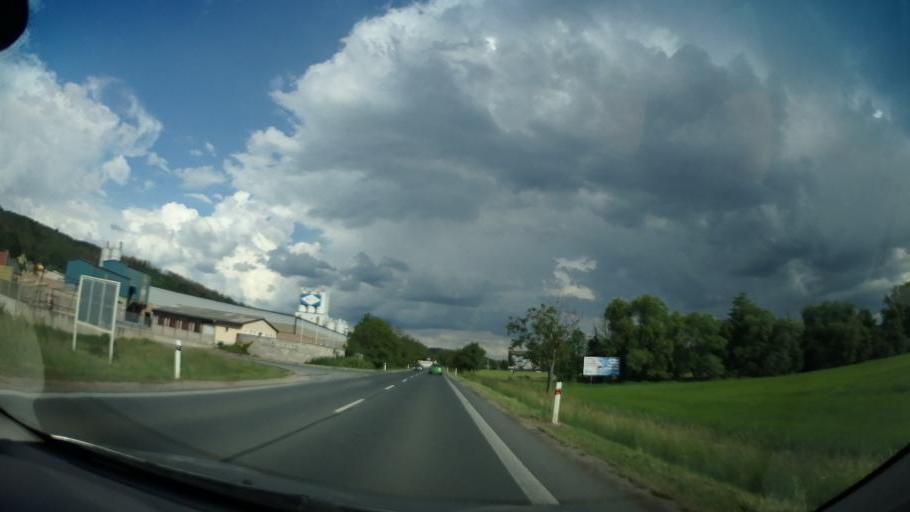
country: CZ
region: South Moravian
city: Tisnov
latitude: 49.3374
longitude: 16.4299
